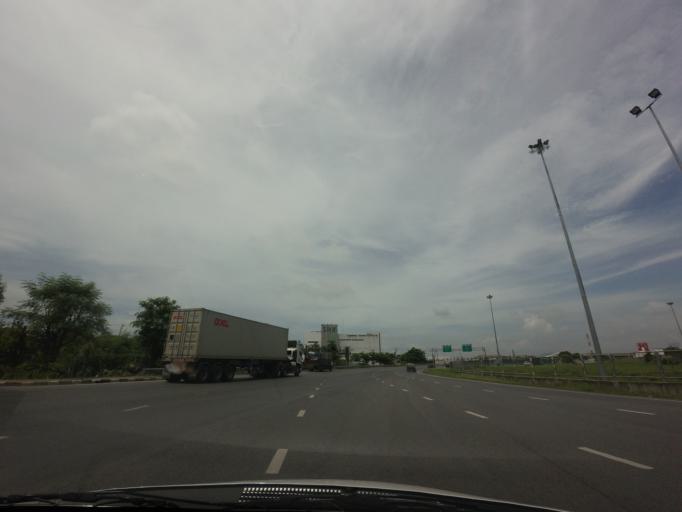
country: TH
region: Bangkok
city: Thung Khru
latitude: 13.6258
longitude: 100.5247
